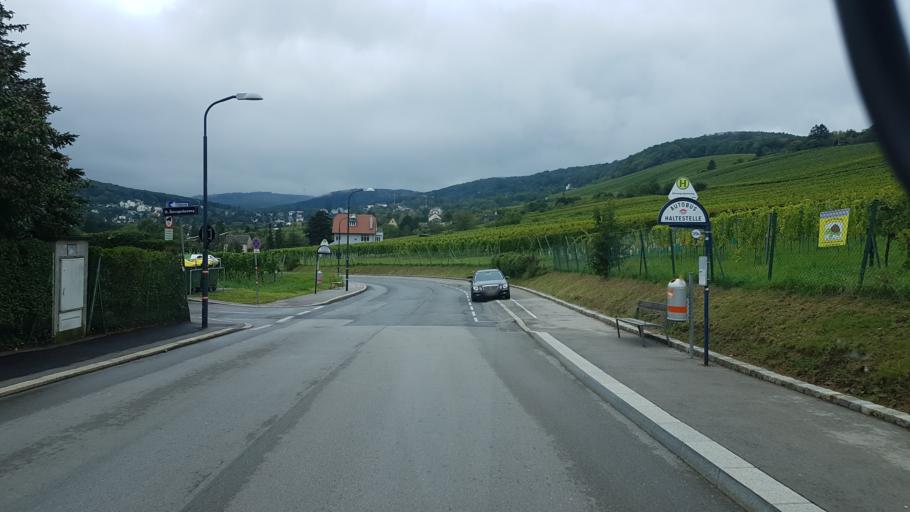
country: AT
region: Lower Austria
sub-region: Politischer Bezirk Wien-Umgebung
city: Klosterneuburg
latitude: 48.2536
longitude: 16.3124
